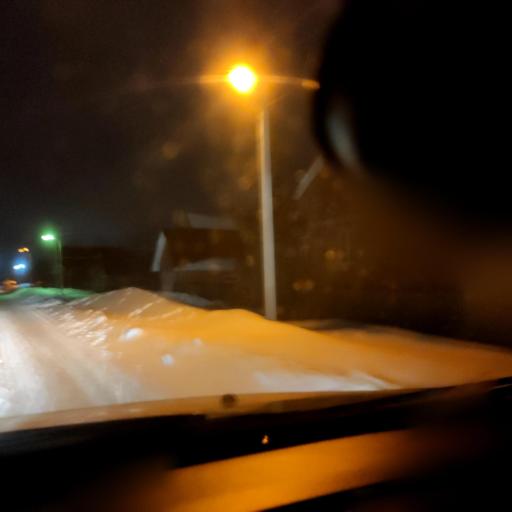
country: RU
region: Bashkortostan
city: Mikhaylovka
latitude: 54.8425
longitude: 55.8314
